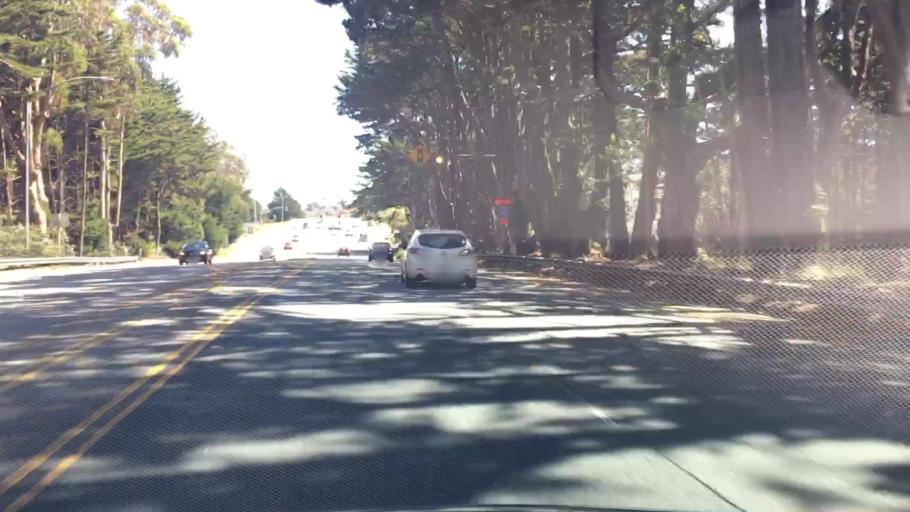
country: US
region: California
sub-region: San Mateo County
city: Pacifica
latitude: 37.6406
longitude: -122.4658
